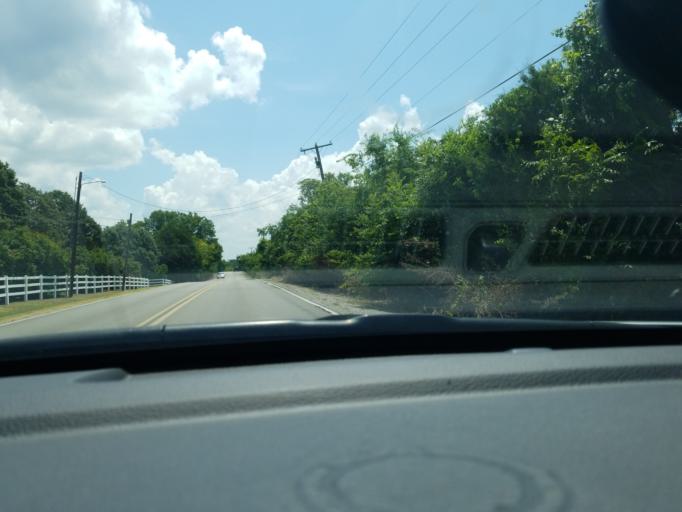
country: US
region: Texas
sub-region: Dallas County
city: Sunnyvale
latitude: 32.8140
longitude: -96.5848
